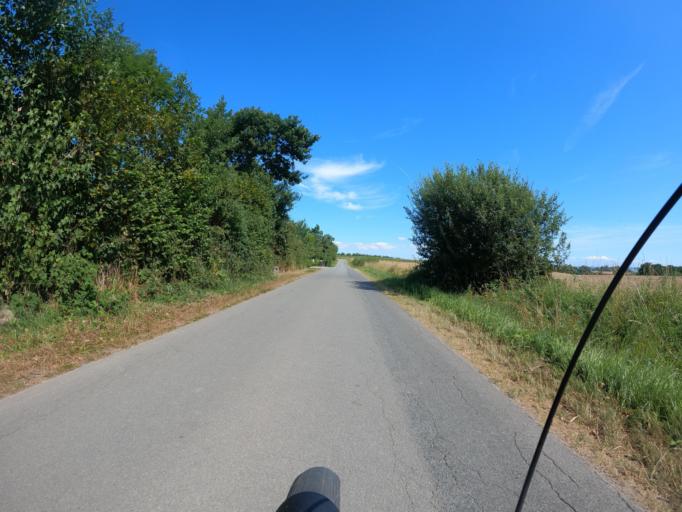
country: DE
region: Schleswig-Holstein
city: Steinbergkirche
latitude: 54.7957
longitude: 9.7450
